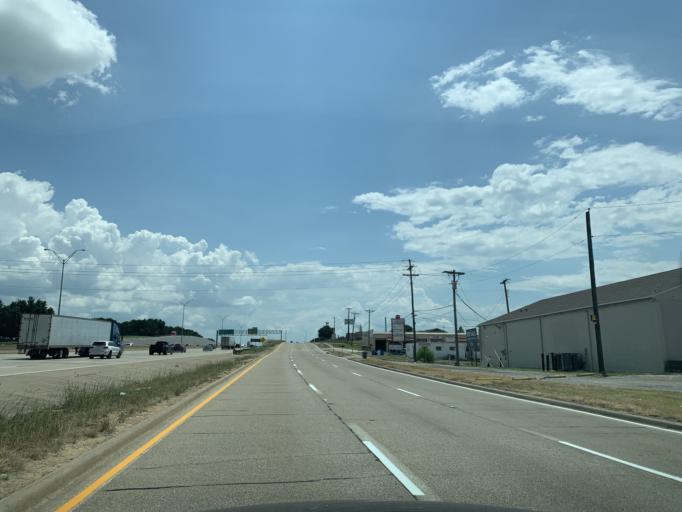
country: US
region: Texas
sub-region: Tarrant County
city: Edgecliff Village
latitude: 32.6600
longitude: -97.3217
